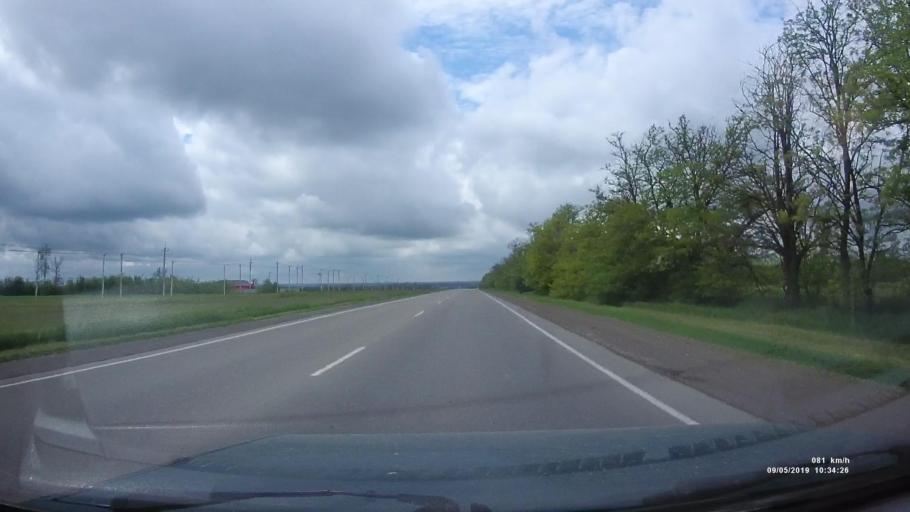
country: RU
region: Rostov
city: Peshkovo
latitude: 47.0542
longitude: 39.4197
